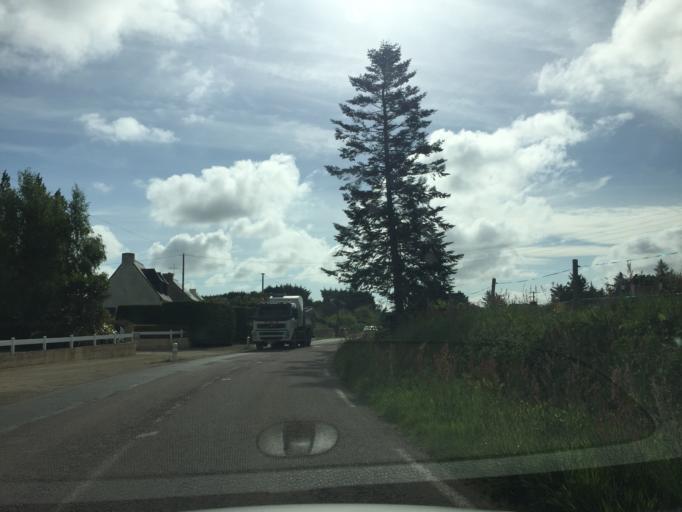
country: FR
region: Brittany
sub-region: Departement des Cotes-d'Armor
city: Matignon
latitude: 48.6240
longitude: -2.3442
